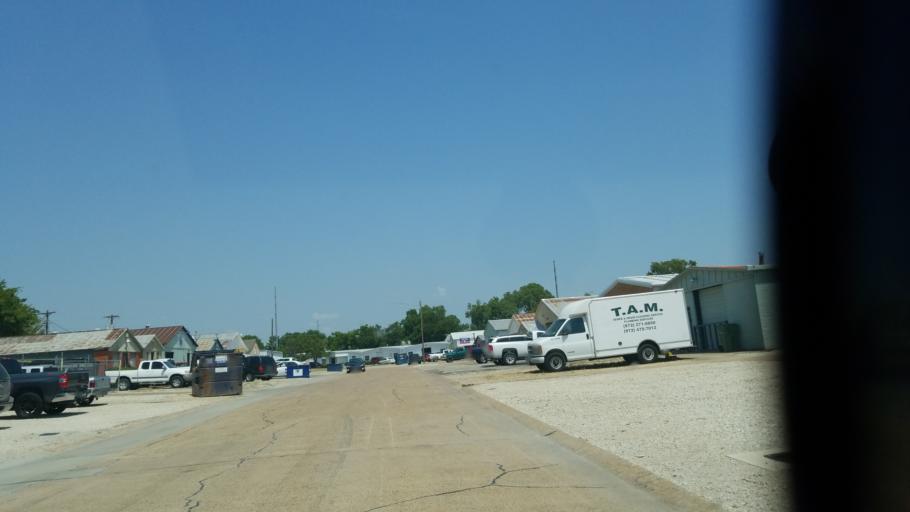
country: US
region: Texas
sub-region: Dallas County
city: Garland
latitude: 32.9120
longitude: -96.6266
